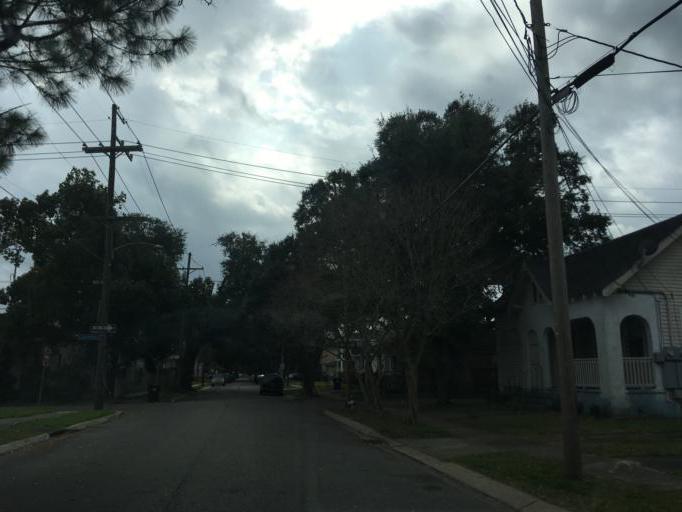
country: US
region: Louisiana
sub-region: Orleans Parish
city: New Orleans
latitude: 29.9940
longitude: -90.0625
